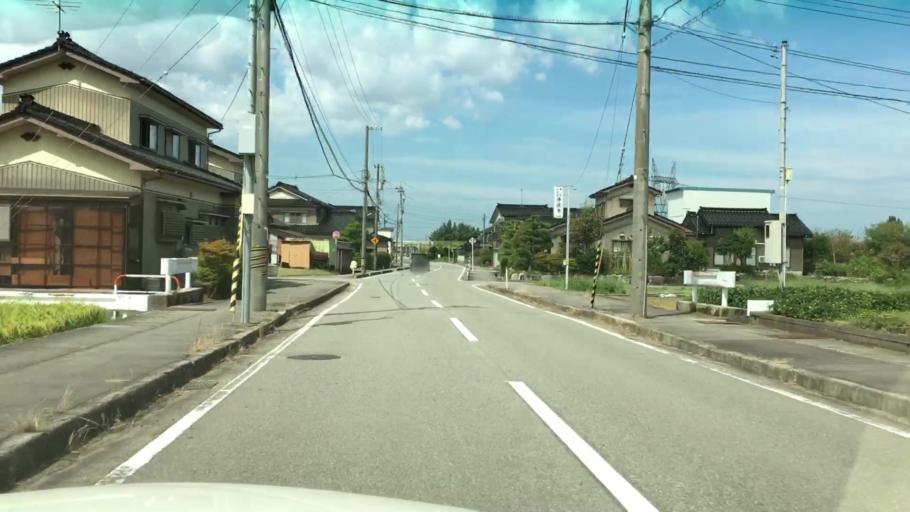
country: JP
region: Toyama
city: Kamiichi
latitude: 36.7062
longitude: 137.3403
